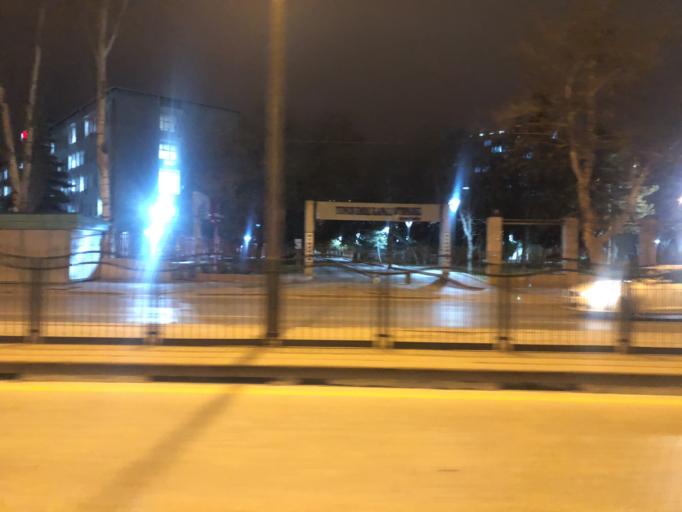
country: TR
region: Ankara
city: Ankara
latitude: 39.9549
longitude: 32.8609
